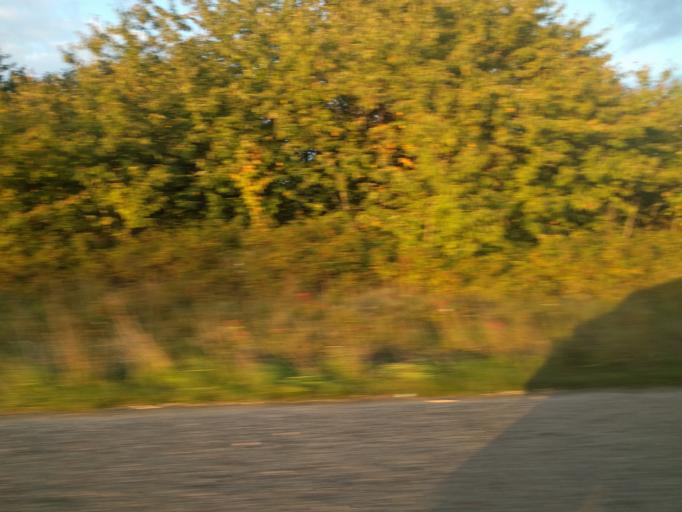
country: DK
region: South Denmark
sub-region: Kerteminde Kommune
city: Langeskov
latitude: 55.3547
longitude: 10.6134
